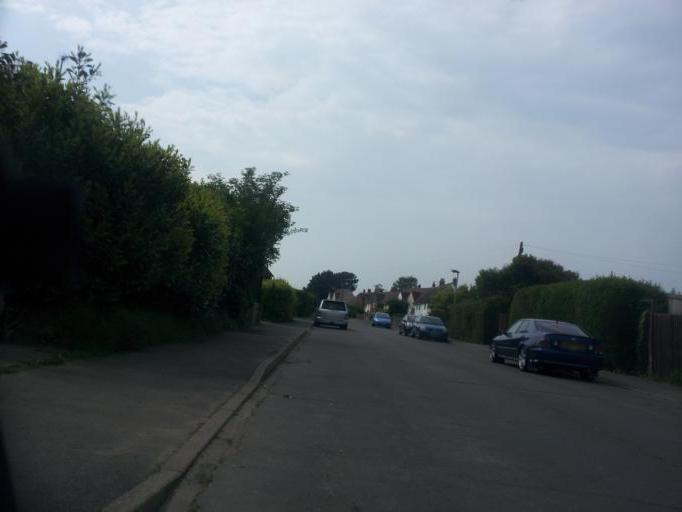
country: GB
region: England
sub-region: Kent
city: West Malling
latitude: 51.2946
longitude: 0.4000
